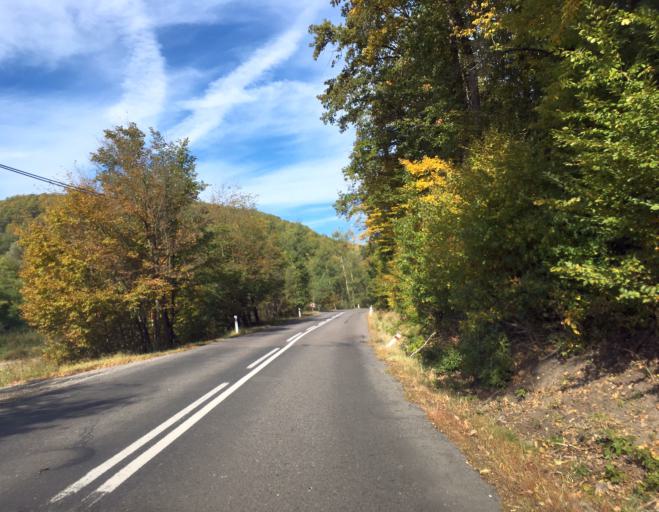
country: SK
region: Banskobystricky
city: Krupina
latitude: 48.3030
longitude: 18.9748
